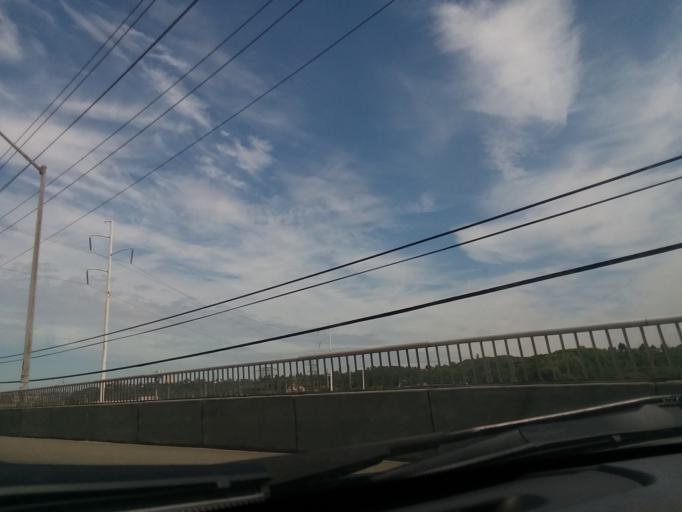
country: US
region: Washington
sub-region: King County
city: Seattle
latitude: 47.5643
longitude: -122.3343
